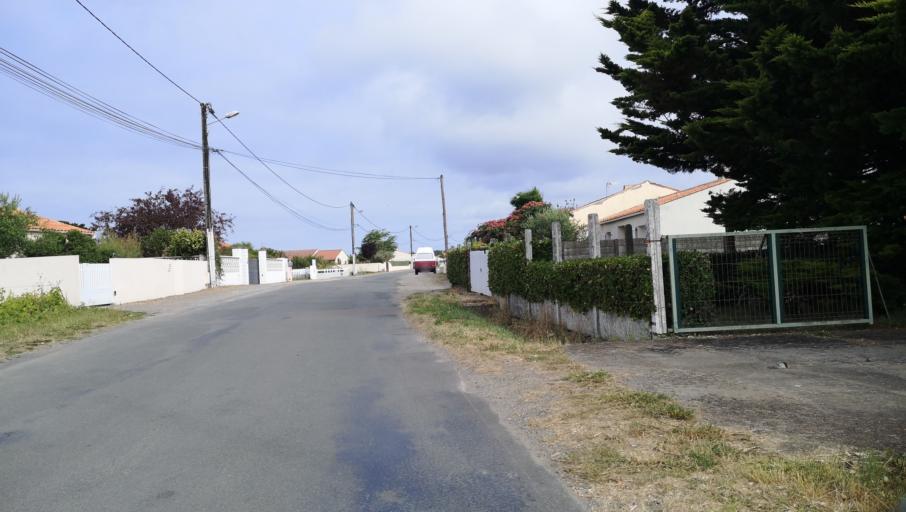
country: FR
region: Pays de la Loire
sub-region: Departement de la Vendee
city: Olonne-sur-Mer
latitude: 46.5499
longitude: -1.8019
